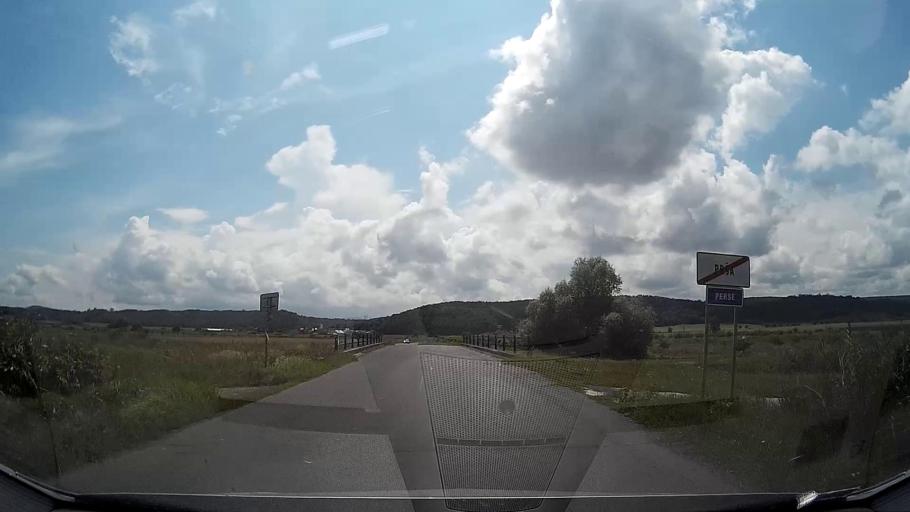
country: SK
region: Banskobystricky
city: Fil'akovo
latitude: 48.2966
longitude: 19.7904
